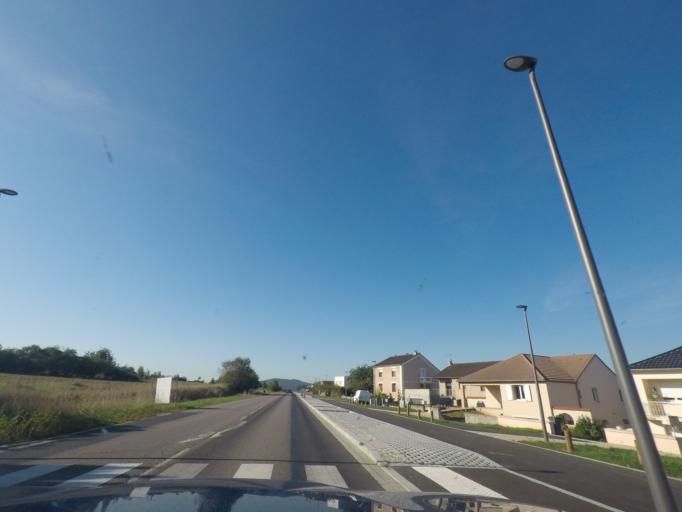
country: FR
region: Lorraine
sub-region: Departement de la Moselle
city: Hettange-Grande
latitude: 49.4180
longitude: 6.1591
